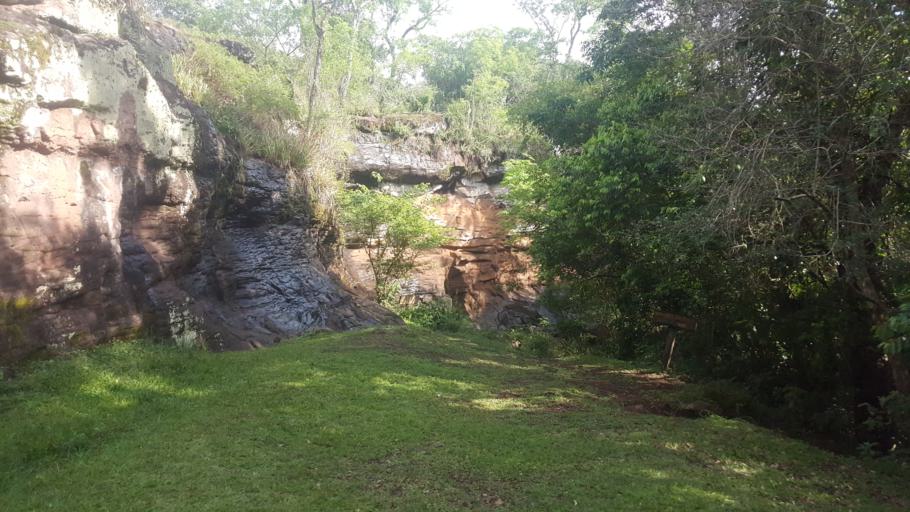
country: AR
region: Misiones
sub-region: Departamento de Candelaria
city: Candelaria
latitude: -27.5602
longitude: -55.7099
